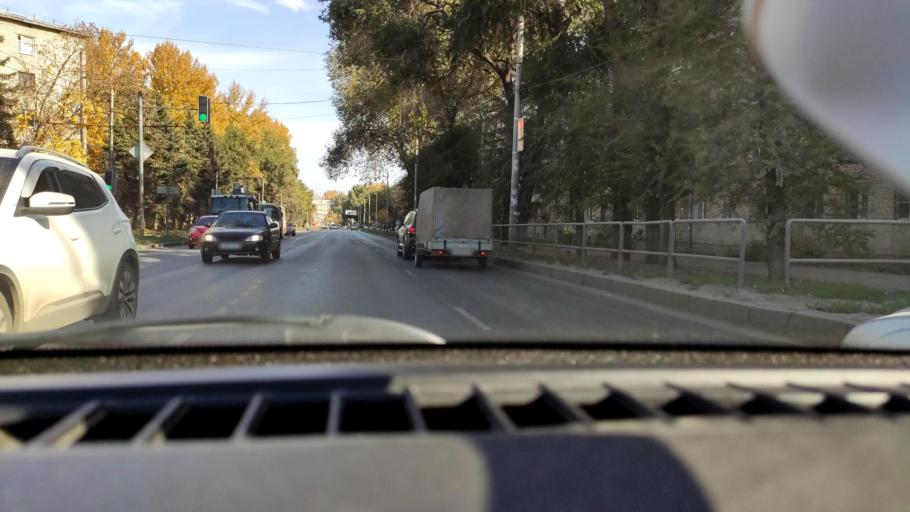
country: RU
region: Samara
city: Samara
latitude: 53.1987
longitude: 50.2236
